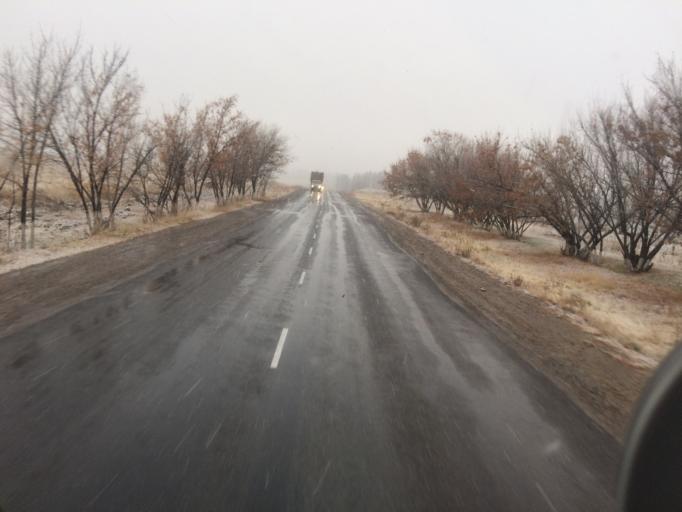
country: KG
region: Chuy
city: Ivanovka
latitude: 42.9651
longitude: 75.0064
